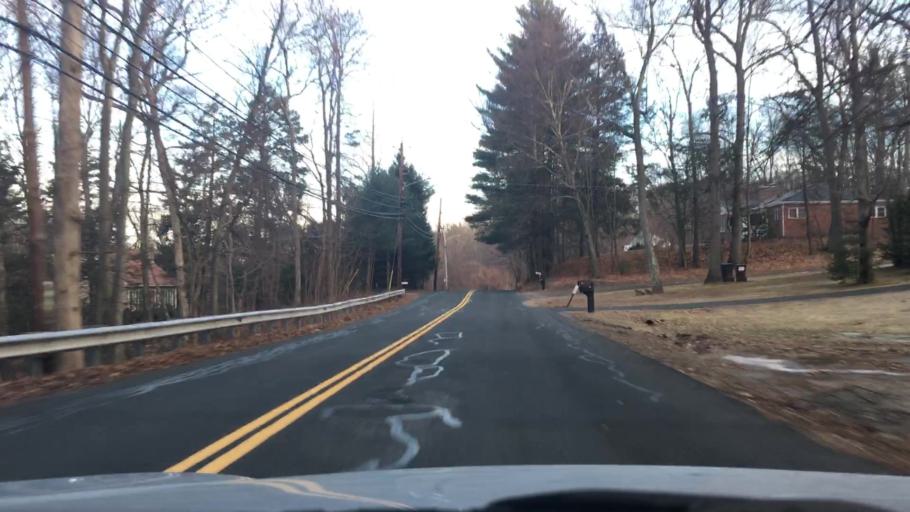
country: US
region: Massachusetts
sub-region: Hampden County
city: Westfield
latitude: 42.0924
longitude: -72.7115
